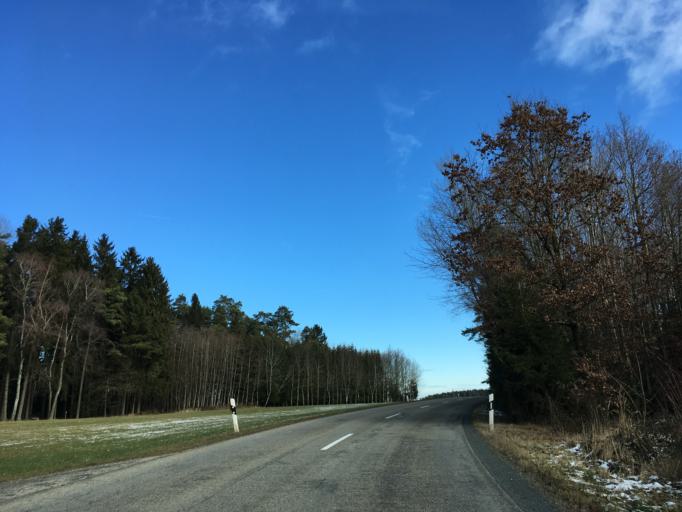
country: DE
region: Bavaria
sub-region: Upper Bavaria
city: Reichertsheim
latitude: 48.2126
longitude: 12.2631
